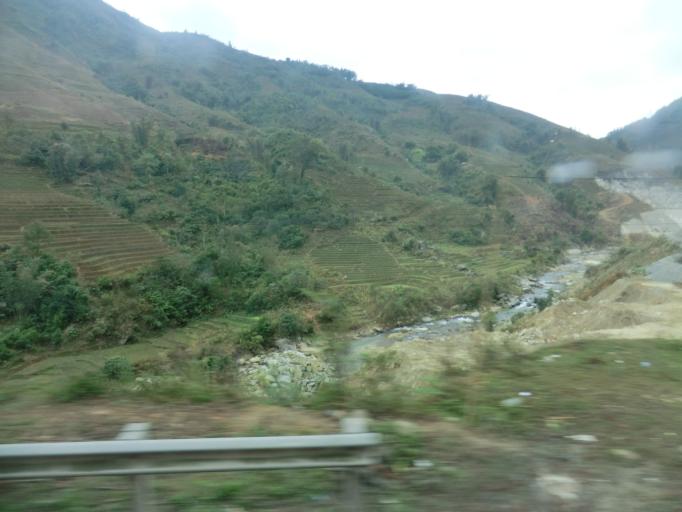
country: VN
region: Lao Cai
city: Lao Cai
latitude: 22.4164
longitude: 103.9091
